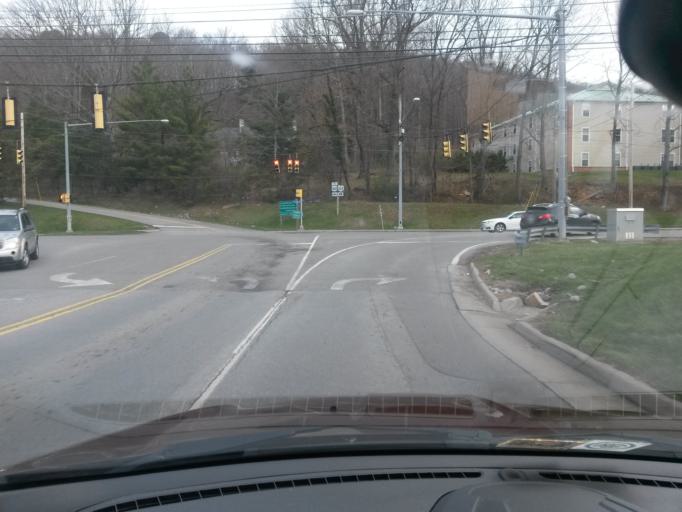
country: US
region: Virginia
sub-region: Tazewell County
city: Bluefield
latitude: 37.2414
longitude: -81.2500
